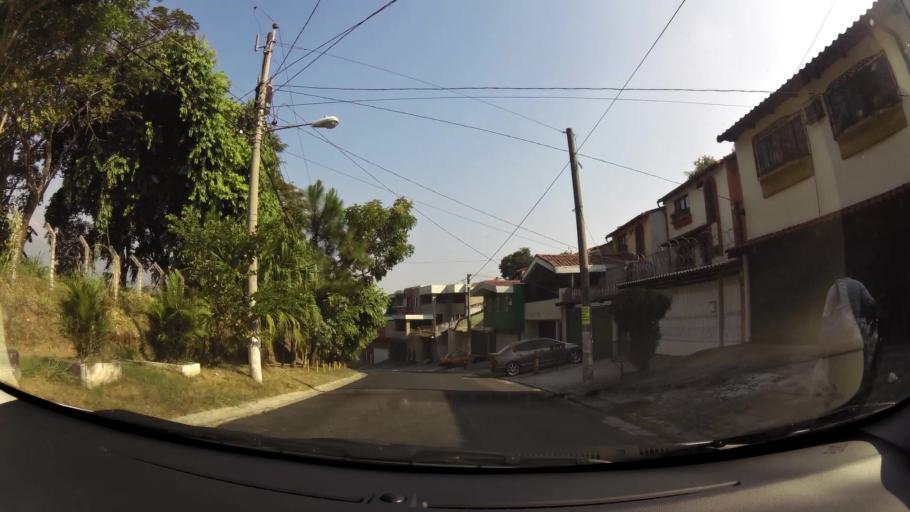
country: SV
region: La Libertad
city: Antiguo Cuscatlan
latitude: 13.6778
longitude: -89.2344
